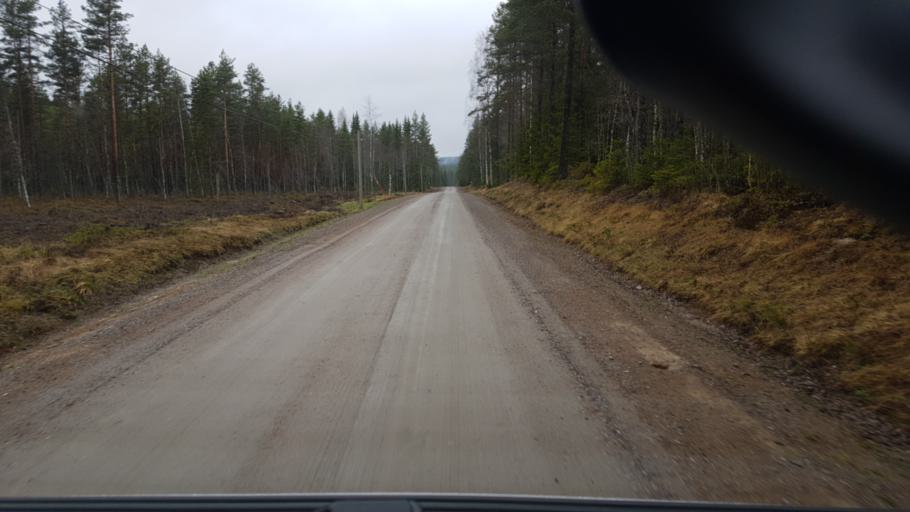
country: SE
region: Vaermland
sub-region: Eda Kommun
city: Charlottenberg
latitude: 59.9634
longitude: 12.5073
